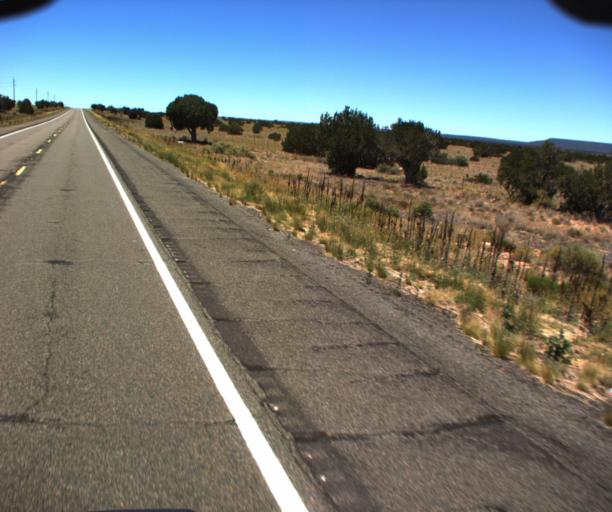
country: US
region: Arizona
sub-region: Coconino County
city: LeChee
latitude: 34.7903
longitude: -110.9913
